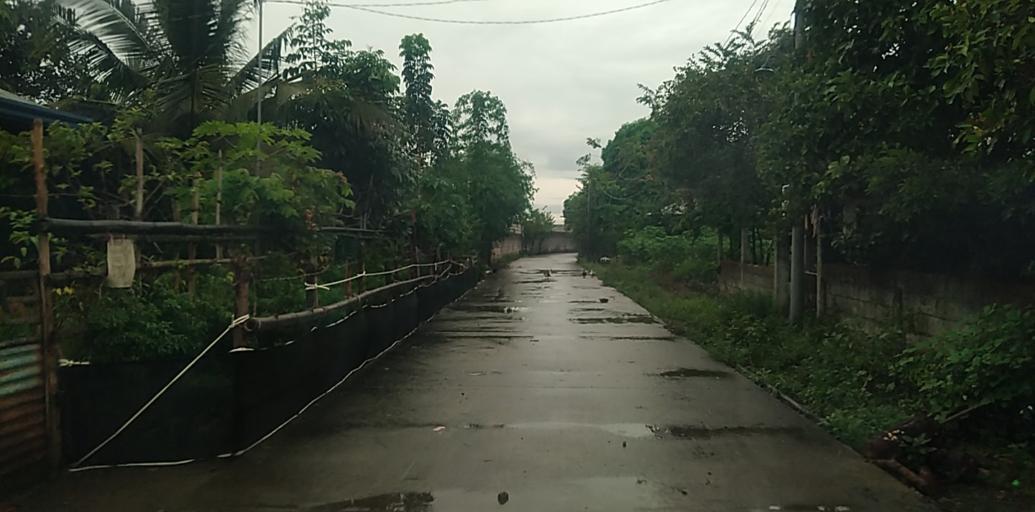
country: PH
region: Central Luzon
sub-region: Province of Pampanga
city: Arayat
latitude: 15.1557
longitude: 120.7388
